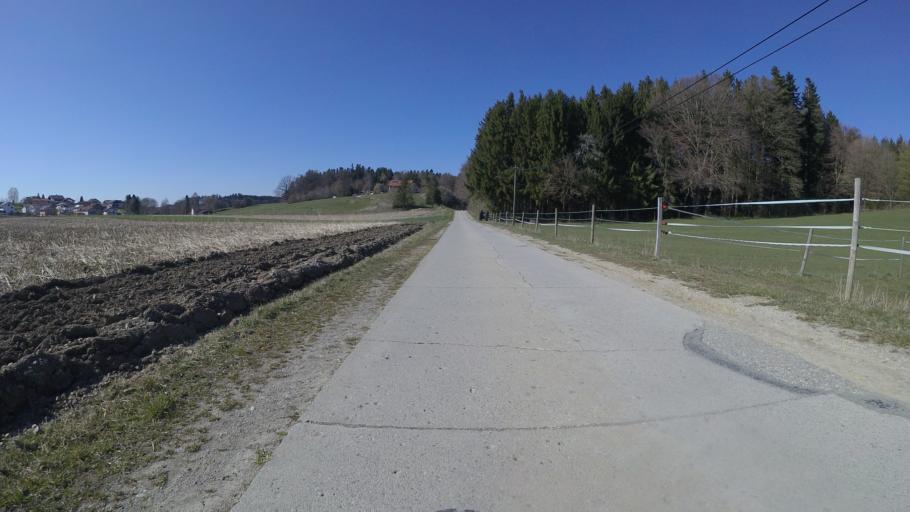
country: DE
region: Bavaria
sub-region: Upper Bavaria
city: Seeon-Seebruck
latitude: 47.9581
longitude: 12.5139
